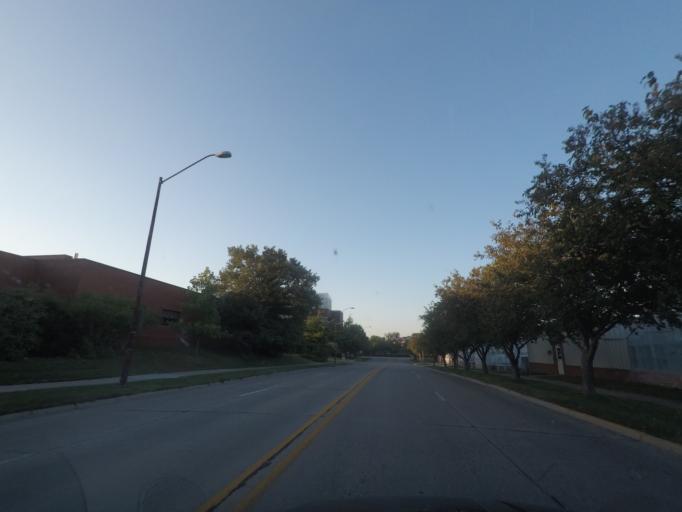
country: US
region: Iowa
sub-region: Story County
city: Ames
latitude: 42.0291
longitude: -93.6415
